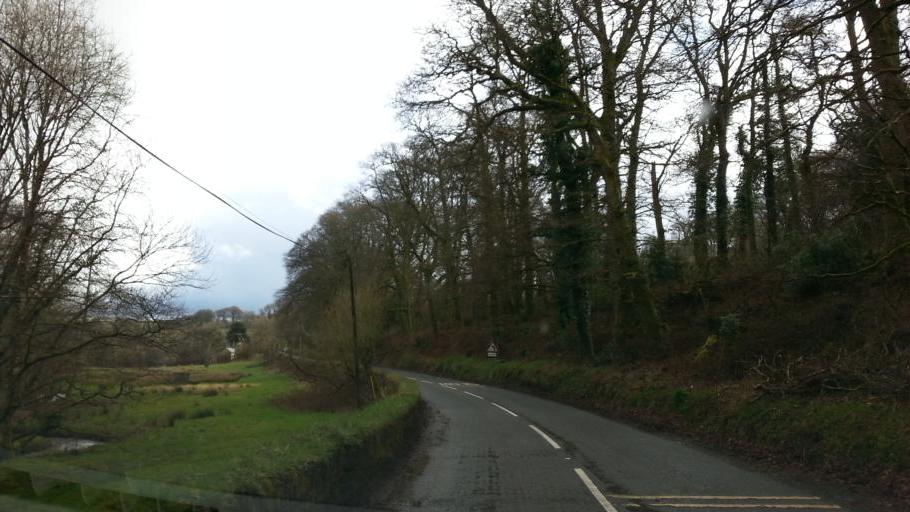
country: GB
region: England
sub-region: Devon
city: Combe Martin
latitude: 51.1509
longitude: -3.9965
